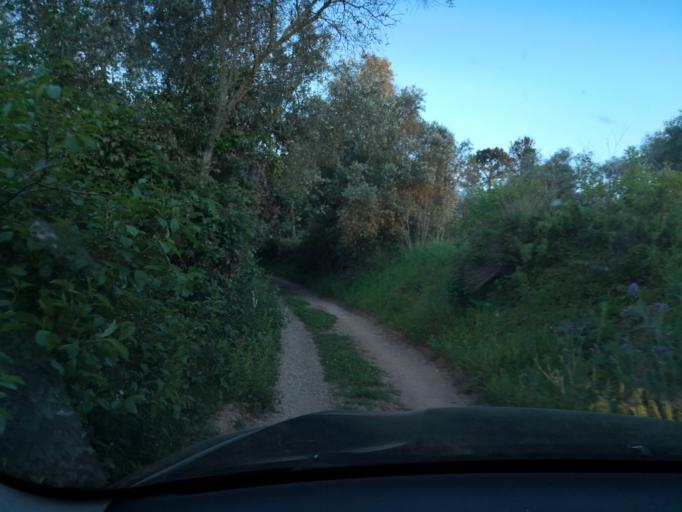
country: PT
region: Setubal
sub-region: Setubal
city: Setubal
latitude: 38.5214
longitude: -8.9234
